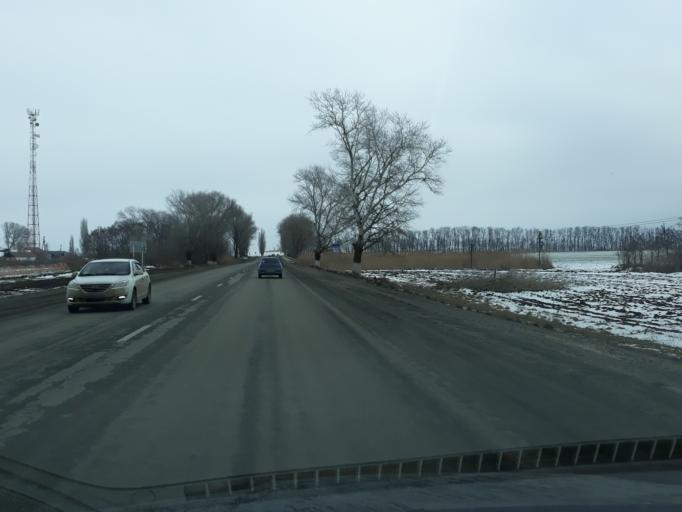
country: RU
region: Rostov
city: Primorka
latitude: 47.3220
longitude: 39.0744
